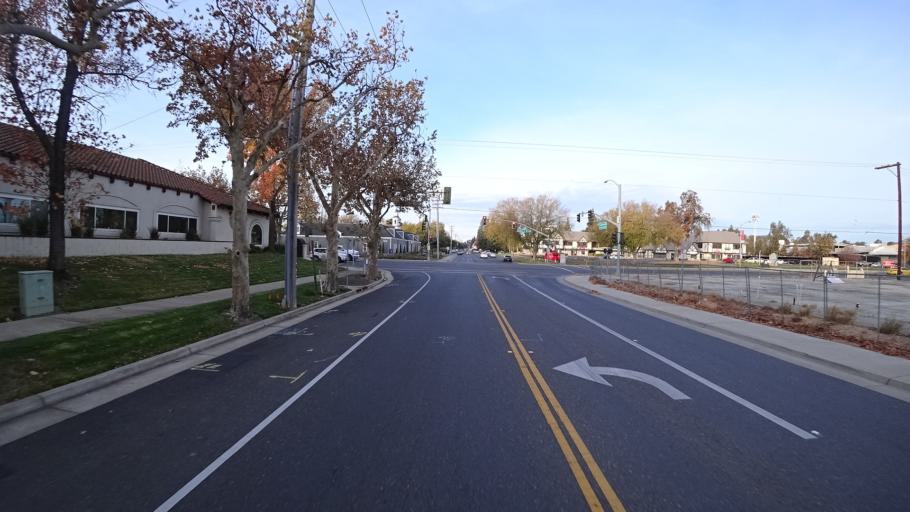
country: US
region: California
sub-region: Sacramento County
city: Citrus Heights
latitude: 38.7184
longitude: -121.2899
